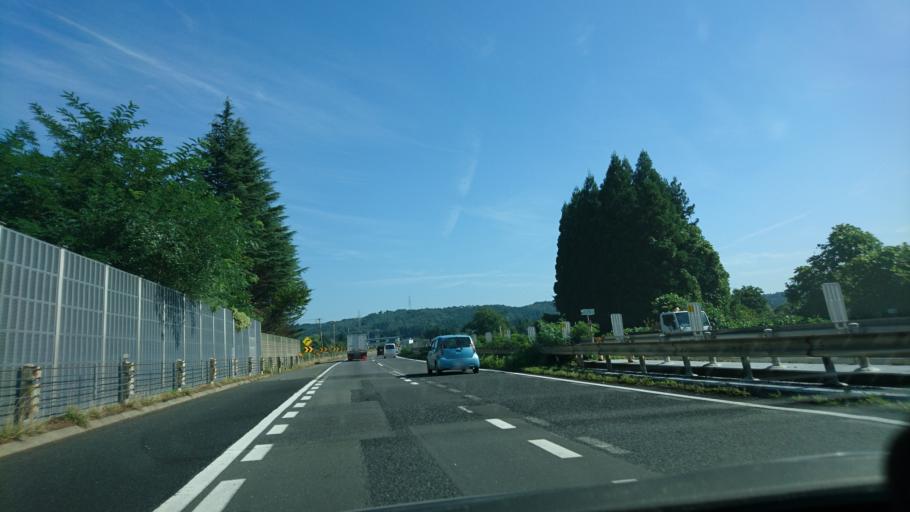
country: JP
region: Iwate
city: Ichinoseki
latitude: 39.0108
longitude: 141.0875
